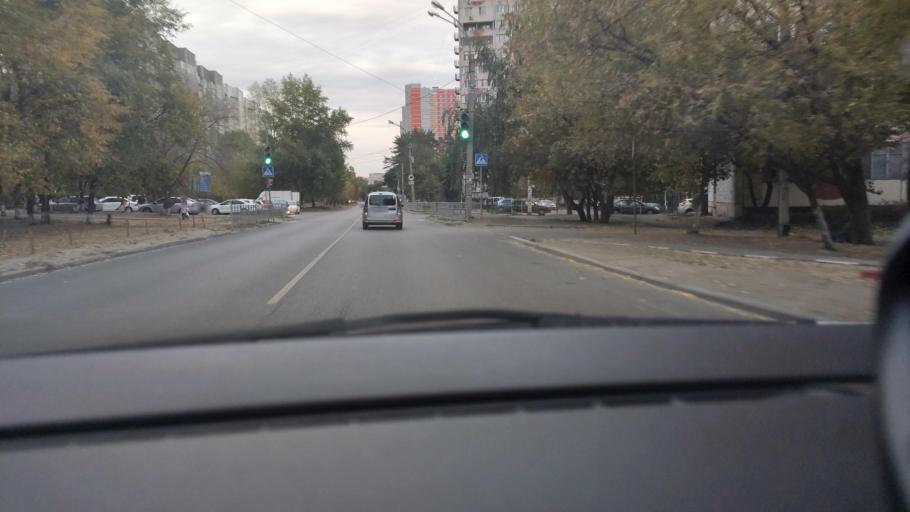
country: RU
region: Voronezj
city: Pridonskoy
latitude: 51.6863
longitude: 39.1260
